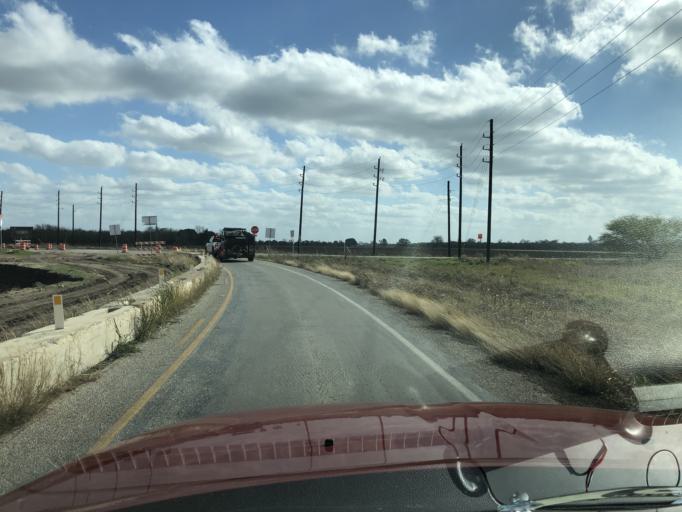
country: US
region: Texas
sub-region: Austin County
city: Sealy
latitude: 29.7726
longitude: -96.0777
